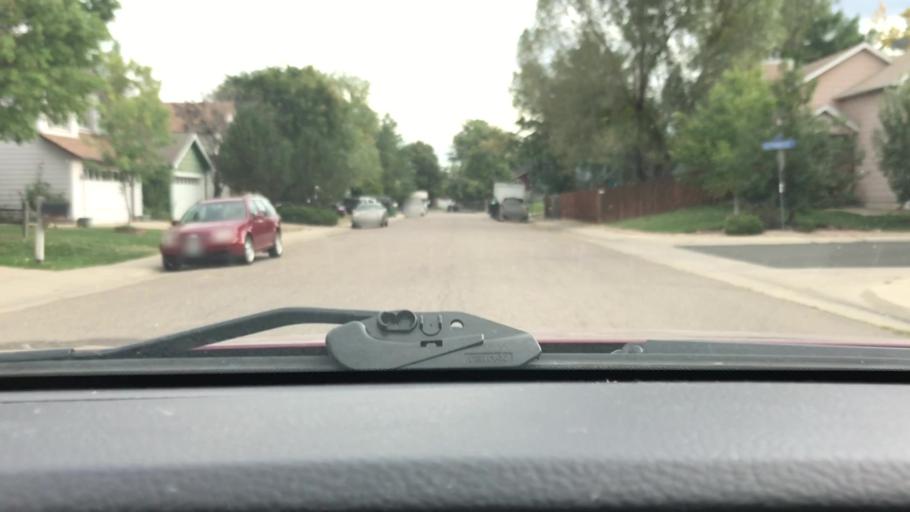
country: US
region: Colorado
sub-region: Broomfield County
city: Broomfield
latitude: 39.9271
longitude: -105.0393
